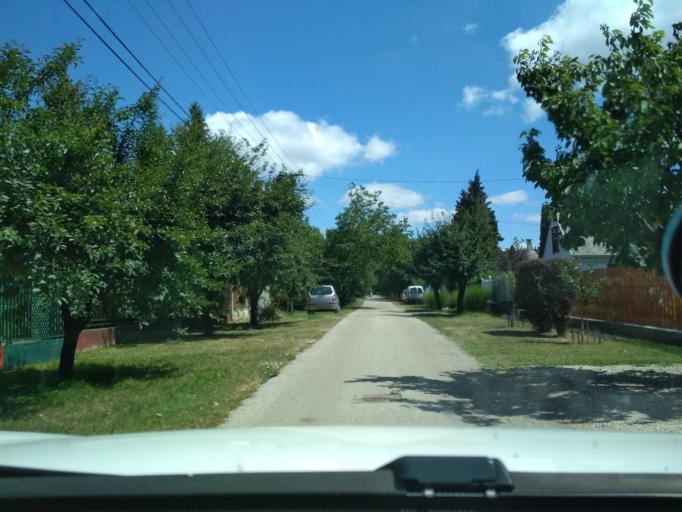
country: HU
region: Fejer
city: Gardony
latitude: 47.2095
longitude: 18.6548
